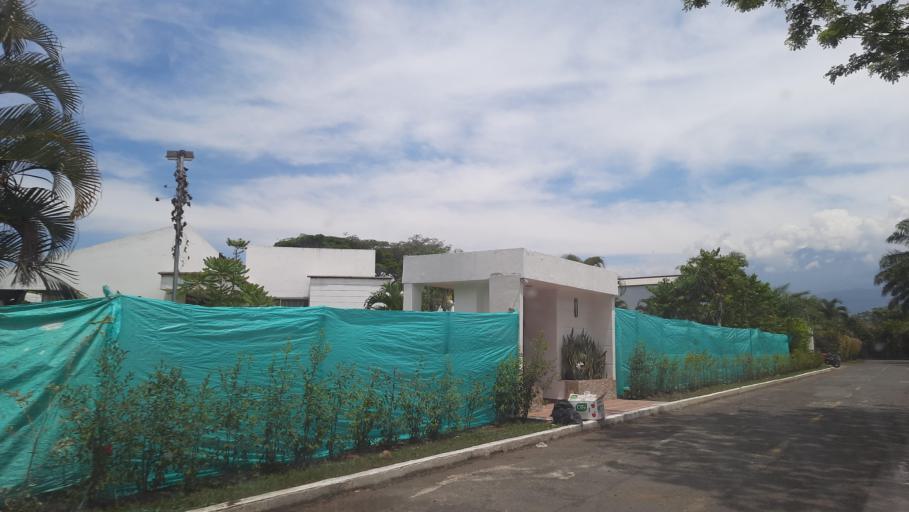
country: CO
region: Valle del Cauca
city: Jamundi
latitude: 3.2678
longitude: -76.5204
